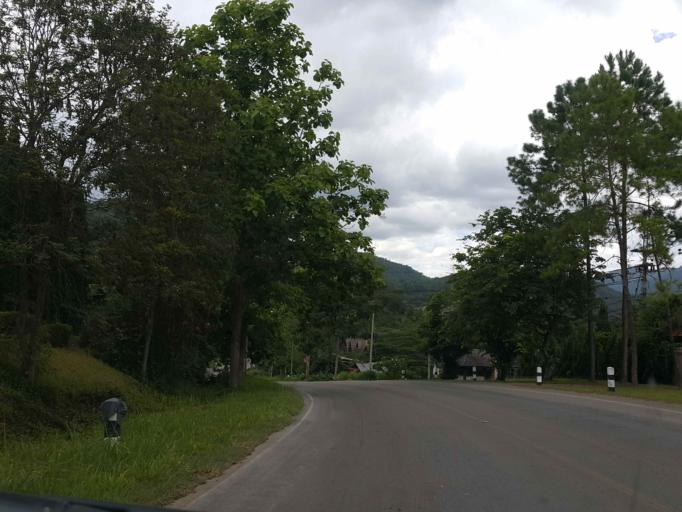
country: TH
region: Chiang Mai
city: Hang Dong
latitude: 18.7840
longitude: 98.8461
